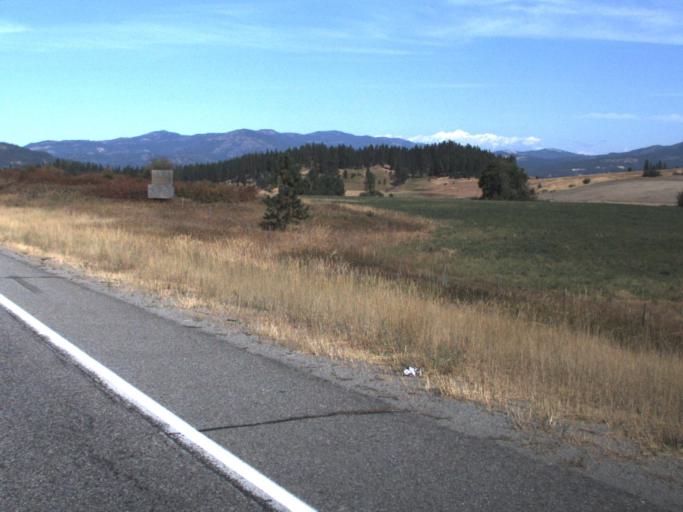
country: US
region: Washington
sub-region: Stevens County
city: Chewelah
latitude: 48.1932
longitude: -117.7029
